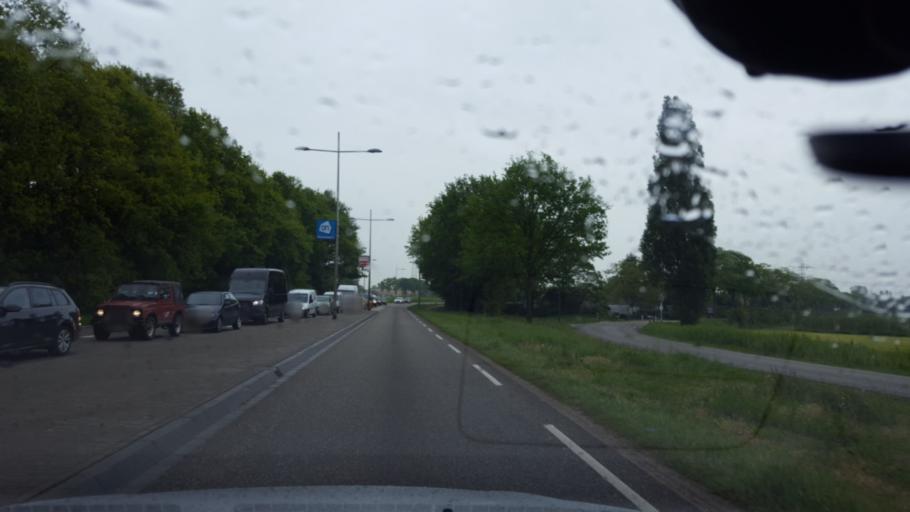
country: NL
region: North Brabant
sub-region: Gemeente Helmond
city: Helmond
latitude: 51.4651
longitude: 5.6625
